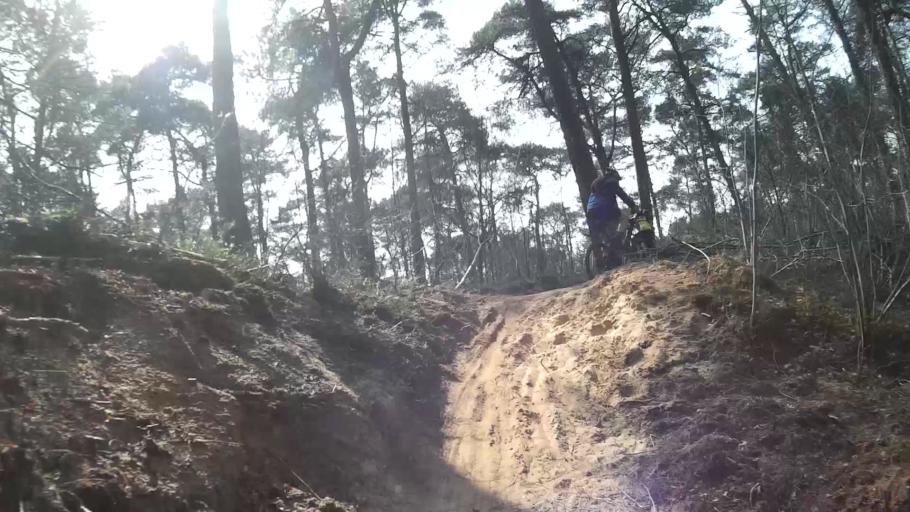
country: NL
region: Utrecht
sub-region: Gemeente Utrechtse Heuvelrug
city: Driebergen-Rijsenburg
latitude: 52.0667
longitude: 5.3125
